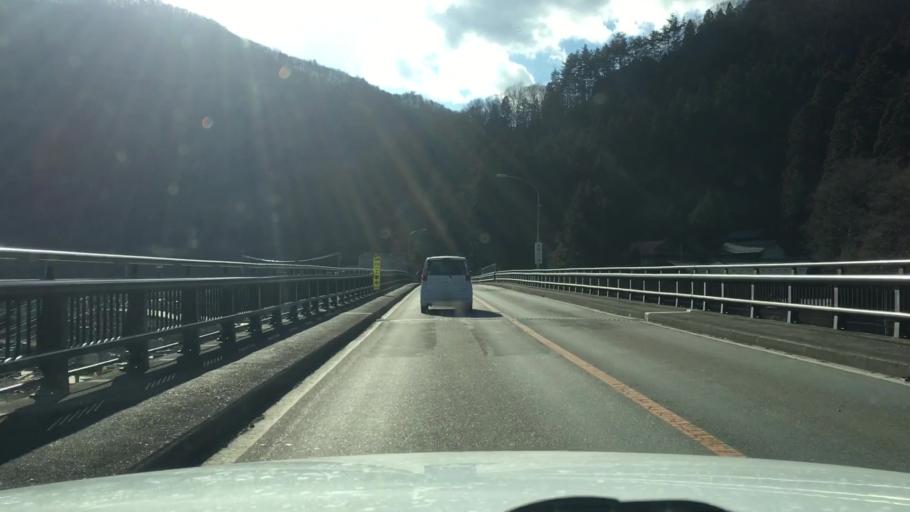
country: JP
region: Iwate
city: Miyako
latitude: 39.6009
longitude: 141.7622
